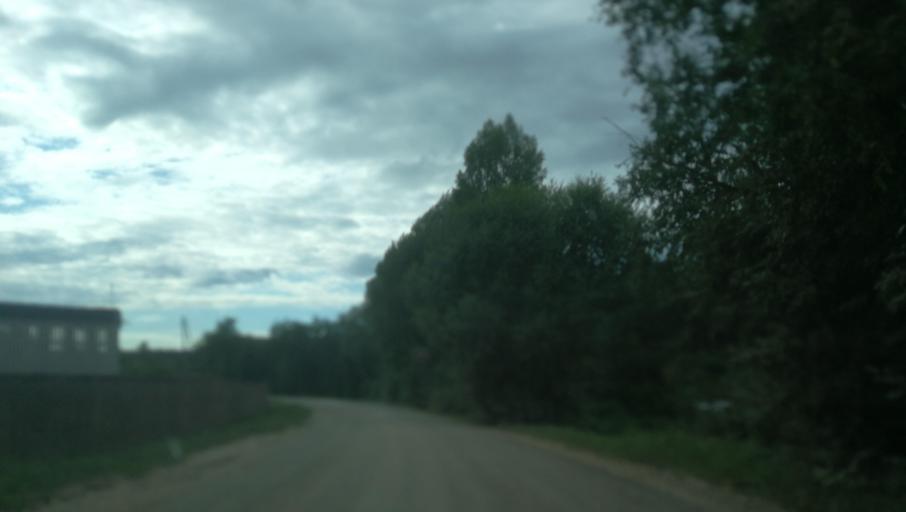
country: LV
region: Cesu Rajons
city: Cesis
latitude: 57.3223
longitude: 25.2675
